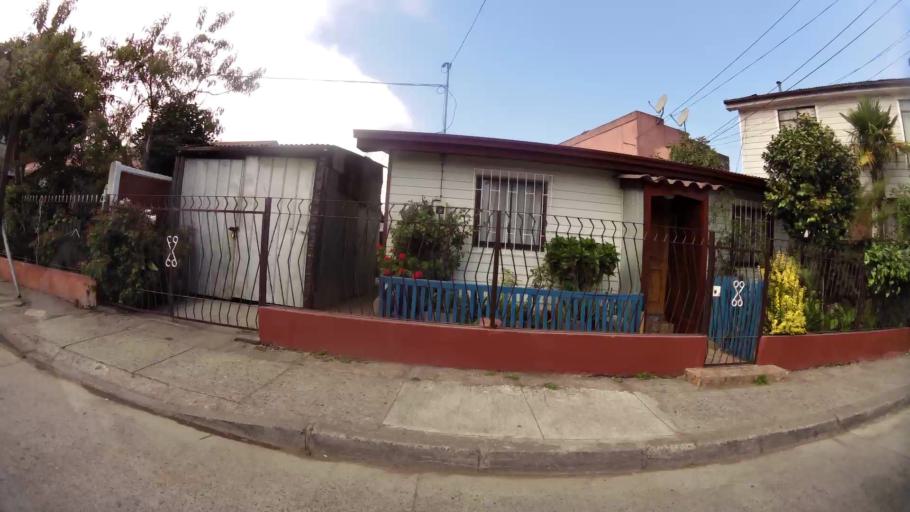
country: CL
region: Biobio
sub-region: Provincia de Concepcion
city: Concepcion
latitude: -36.8052
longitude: -73.0426
